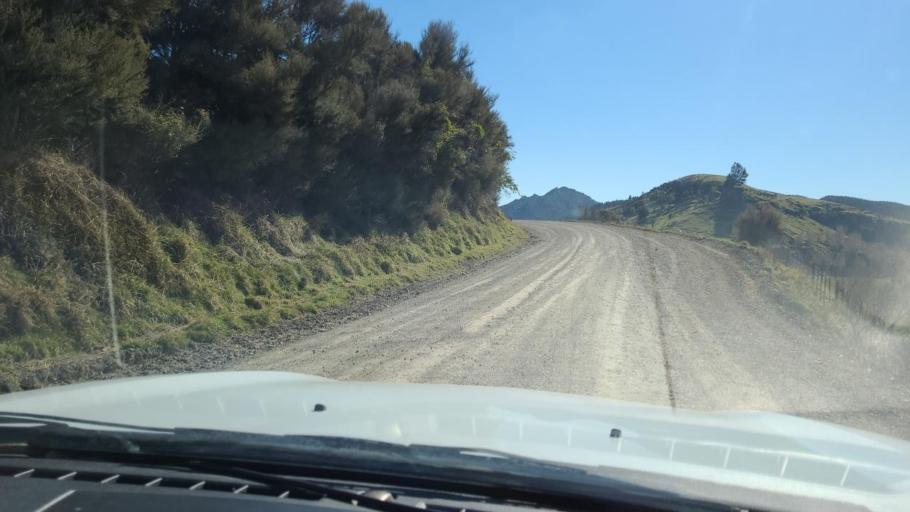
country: NZ
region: Hawke's Bay
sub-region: Napier City
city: Taradale
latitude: -39.4702
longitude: 176.4079
